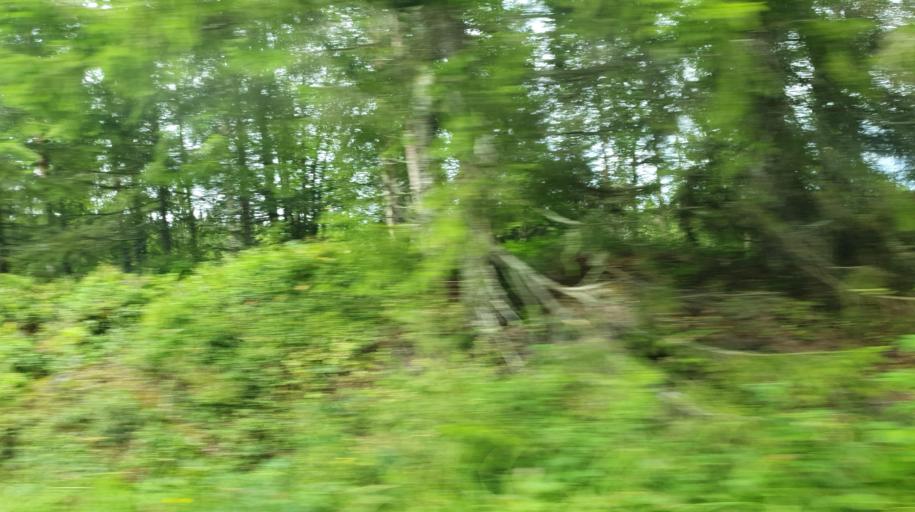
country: NO
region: Nord-Trondelag
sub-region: Levanger
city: Skogn
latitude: 63.5596
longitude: 11.1740
